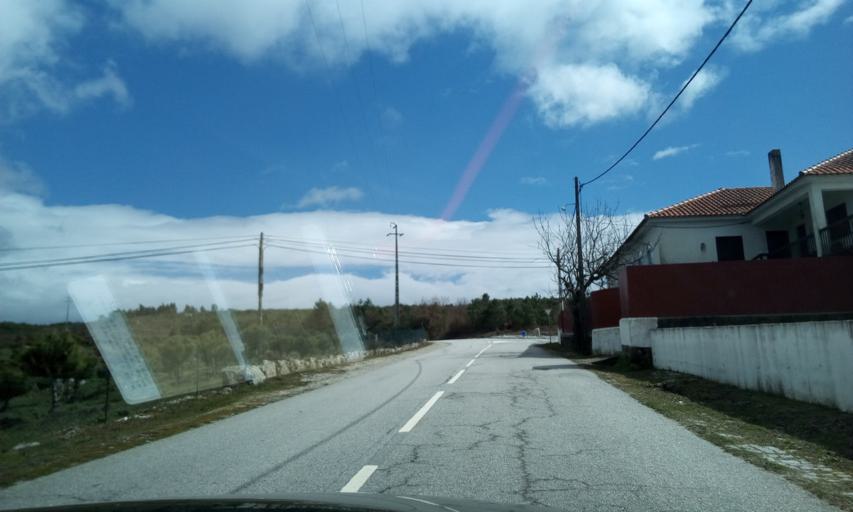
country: PT
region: Guarda
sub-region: Fornos de Algodres
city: Fornos de Algodres
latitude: 40.6394
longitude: -7.5485
